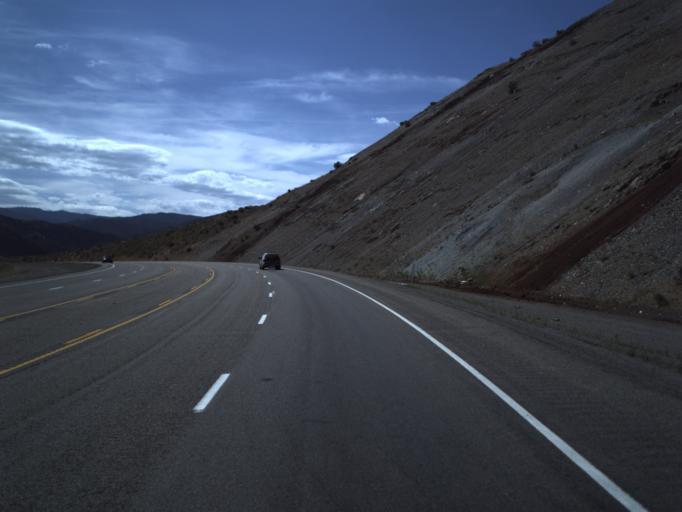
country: US
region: Utah
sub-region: Utah County
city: Mapleton
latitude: 40.0041
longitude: -111.4916
